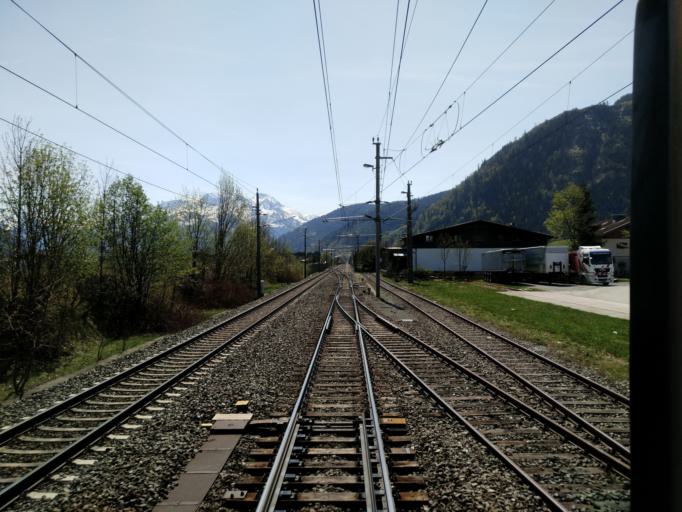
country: AT
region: Salzburg
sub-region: Politischer Bezirk Zell am See
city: Maishofen
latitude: 47.3569
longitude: 12.8091
